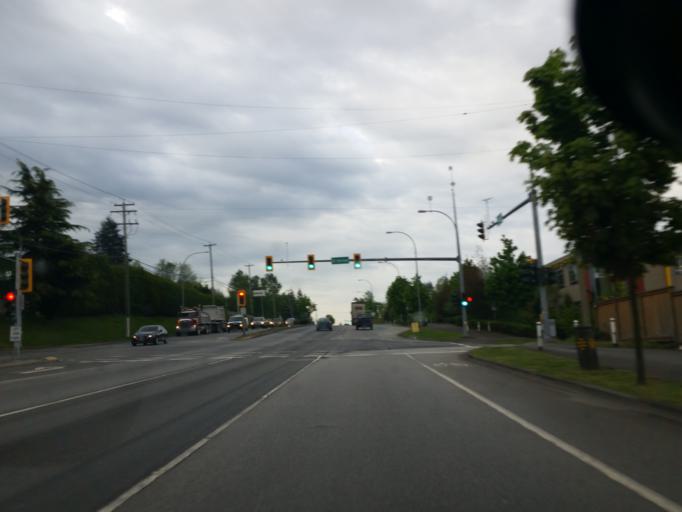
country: CA
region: British Columbia
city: Walnut Grove
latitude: 49.1524
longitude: -122.6684
